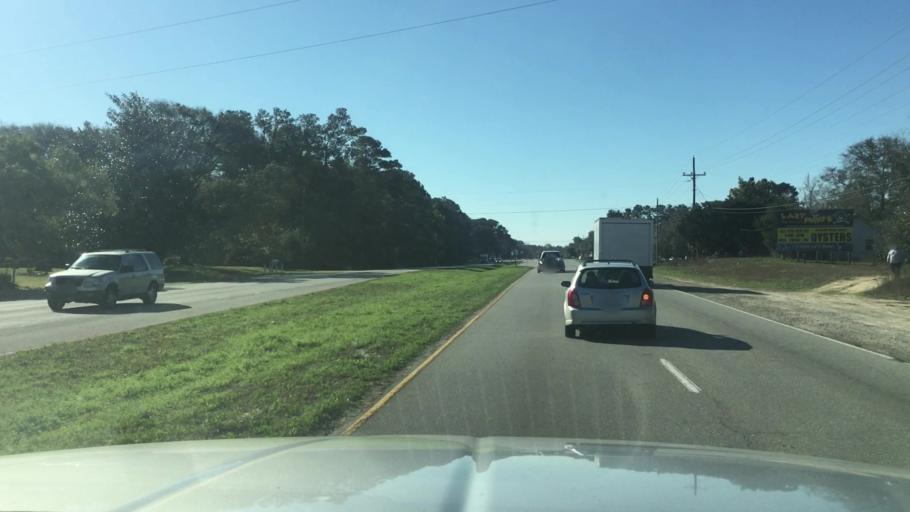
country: US
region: North Carolina
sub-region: New Hanover County
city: Sea Breeze
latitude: 34.0887
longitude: -77.8965
